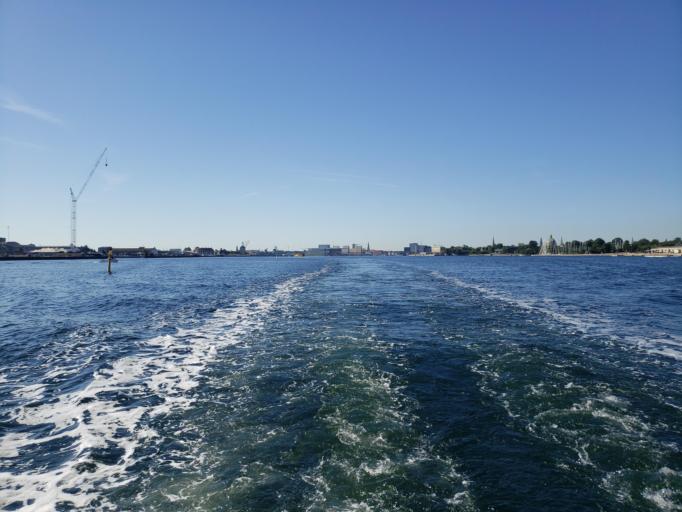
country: DK
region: Capital Region
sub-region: Kobenhavn
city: Christianshavn
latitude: 55.6995
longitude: 12.6063
